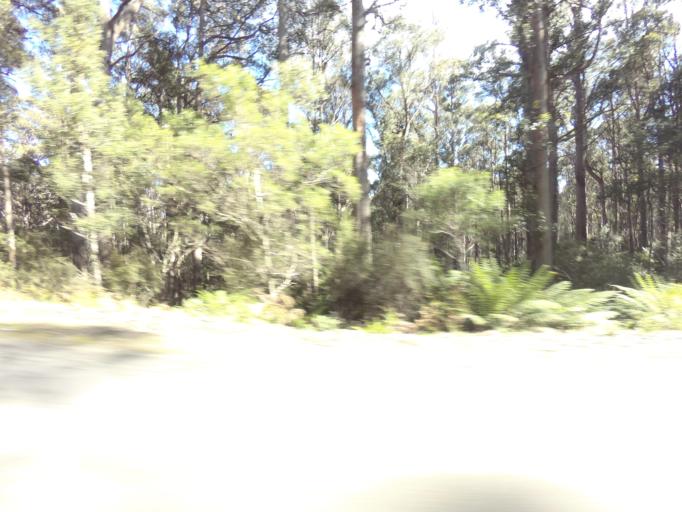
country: AU
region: Tasmania
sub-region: Derwent Valley
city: New Norfolk
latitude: -42.7393
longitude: 146.6622
